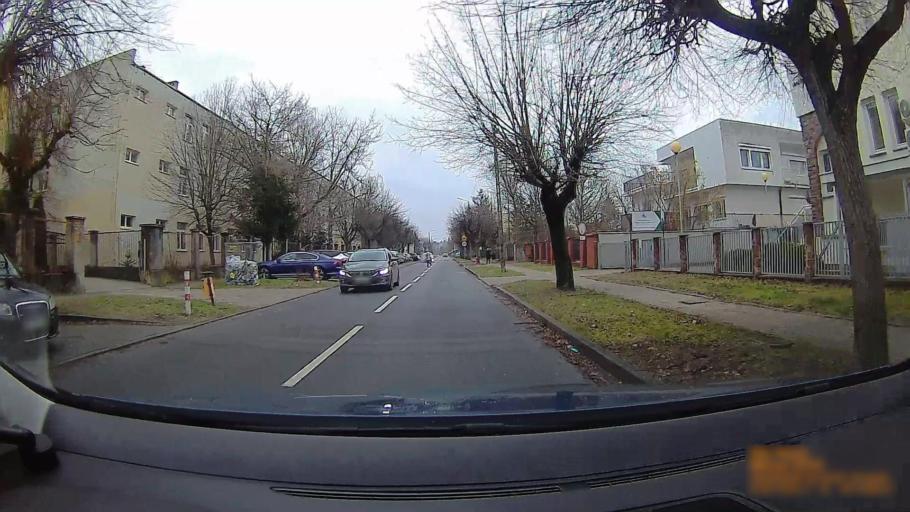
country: PL
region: Greater Poland Voivodeship
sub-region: Konin
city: Konin
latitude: 52.2114
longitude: 18.2484
